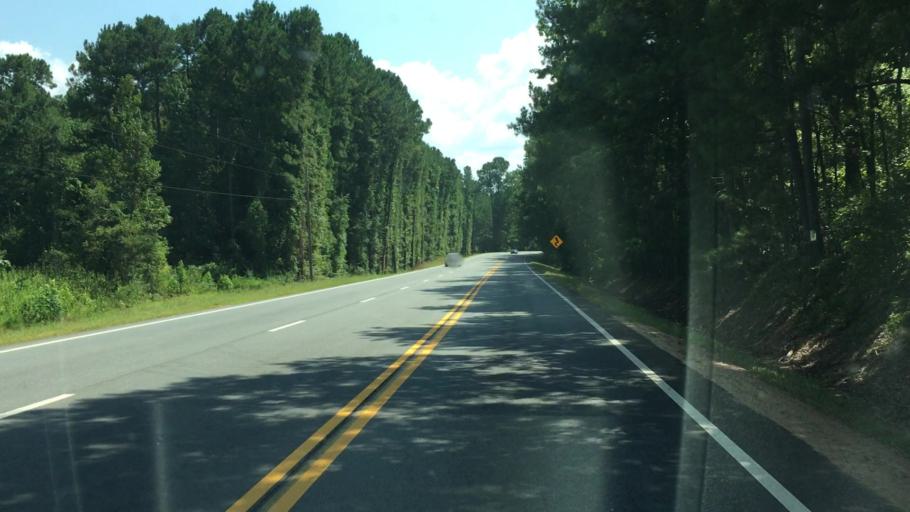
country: US
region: Georgia
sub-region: Oconee County
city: Watkinsville
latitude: 33.7300
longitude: -83.4307
